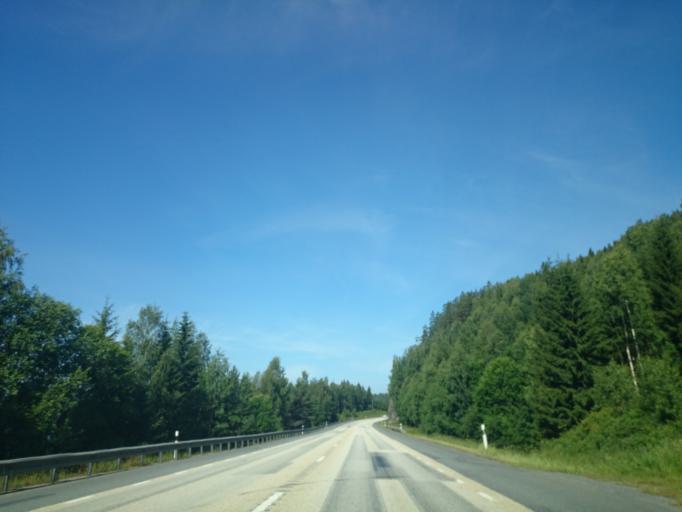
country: SE
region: Vaesternorrland
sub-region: Sundsvalls Kommun
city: Matfors
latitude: 62.3851
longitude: 16.7852
